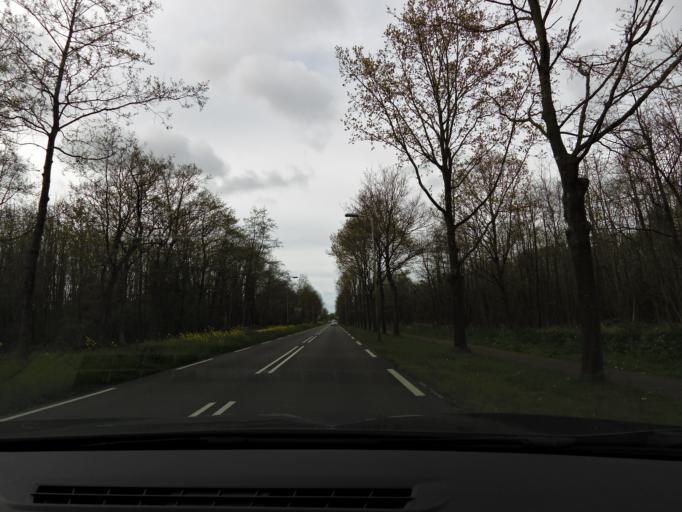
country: NL
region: South Holland
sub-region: Gemeente Lisse
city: Lisse
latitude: 52.2728
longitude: 4.5390
